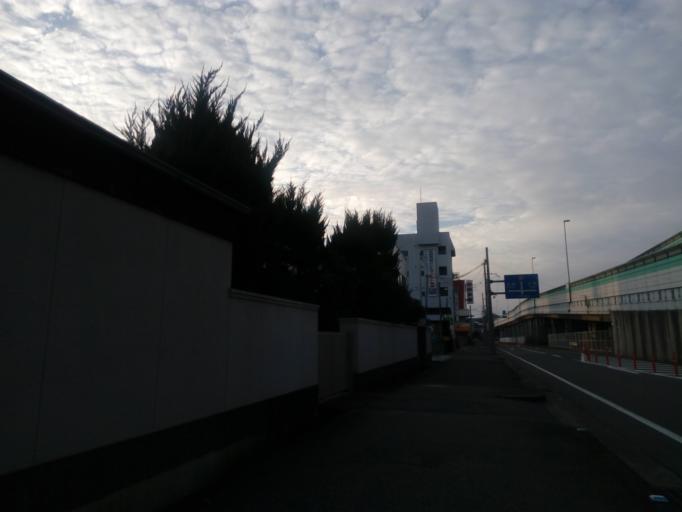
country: JP
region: Hyogo
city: Himeji
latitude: 34.8120
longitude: 134.6813
